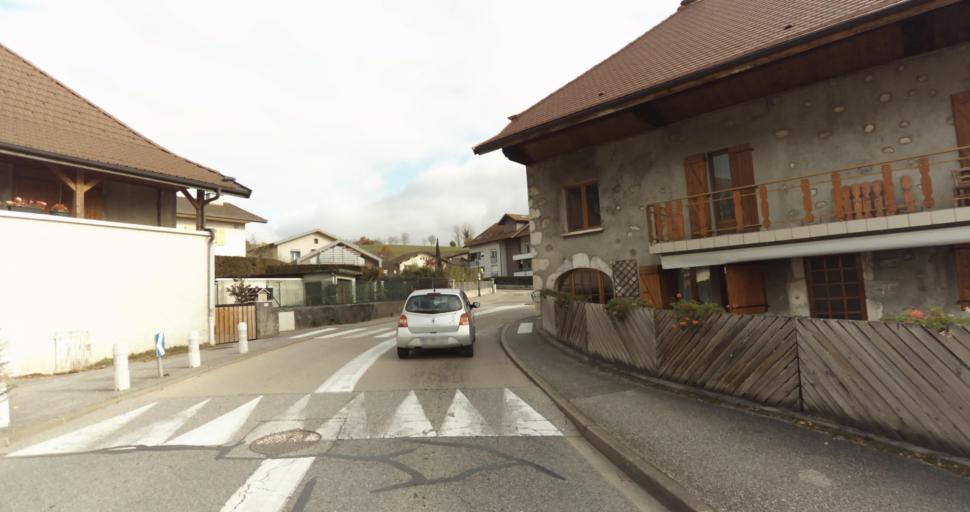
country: FR
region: Rhone-Alpes
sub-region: Departement de la Haute-Savoie
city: Epagny
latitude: 45.9396
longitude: 6.0924
